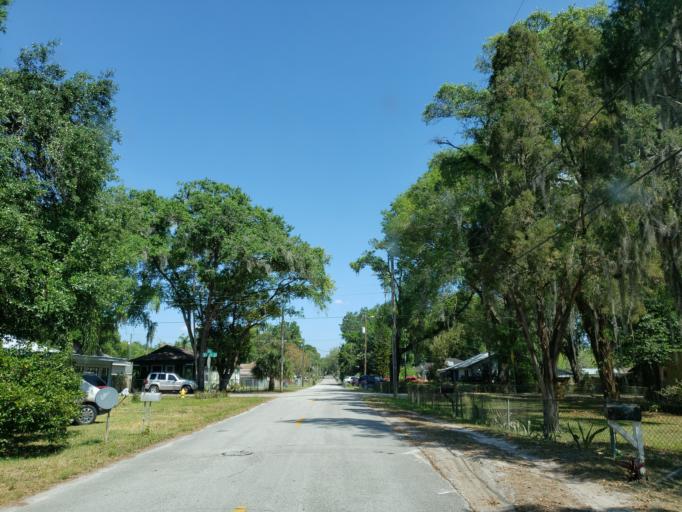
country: US
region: Florida
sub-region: Hillsborough County
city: Plant City
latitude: 28.0234
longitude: -82.1314
